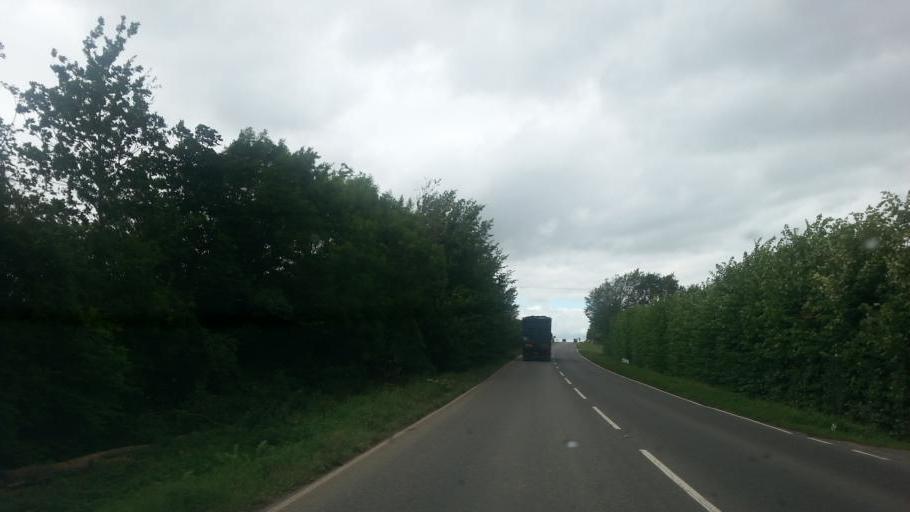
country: GB
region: England
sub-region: Cambridgeshire
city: Godmanchester
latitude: 52.2954
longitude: -0.1519
